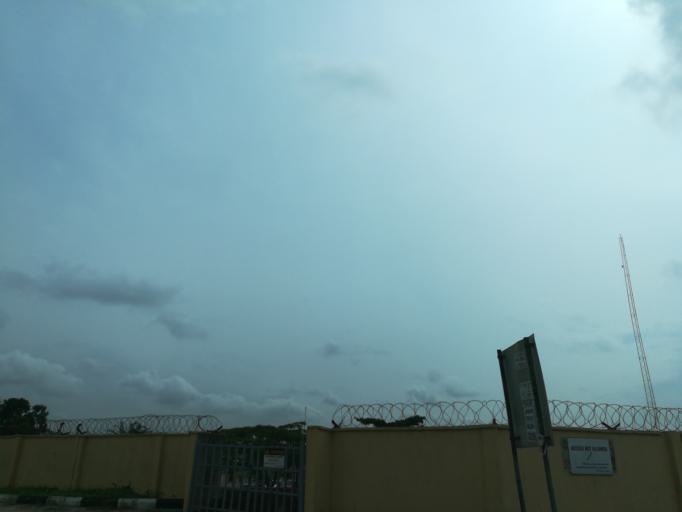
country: NG
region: Lagos
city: Oshodi
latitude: 6.5660
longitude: 3.3236
